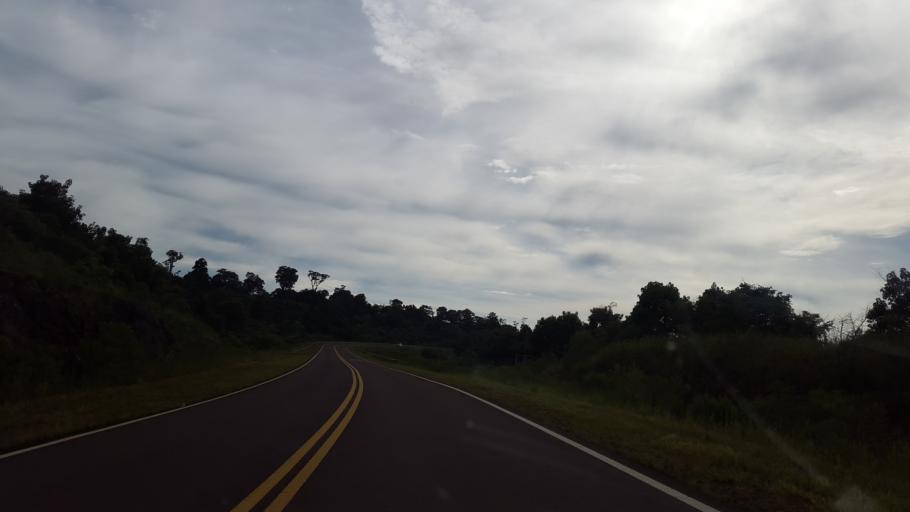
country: AR
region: Misiones
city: Bernardo de Irigoyen
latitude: -26.3853
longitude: -53.7983
